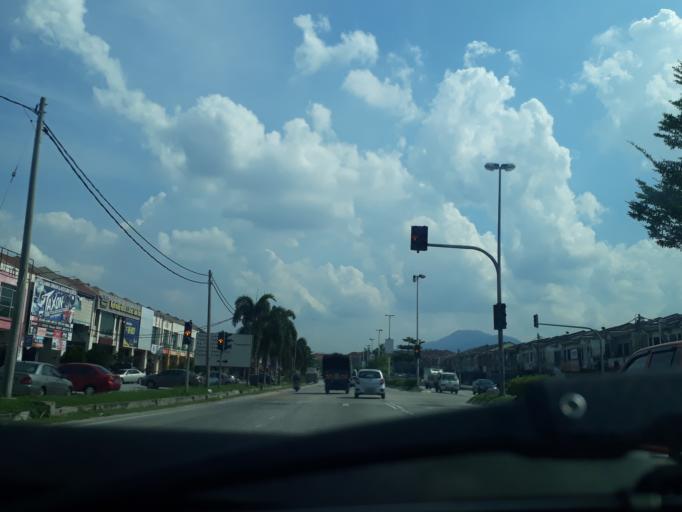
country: MY
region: Perak
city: Ipoh
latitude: 4.6421
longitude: 101.0959
